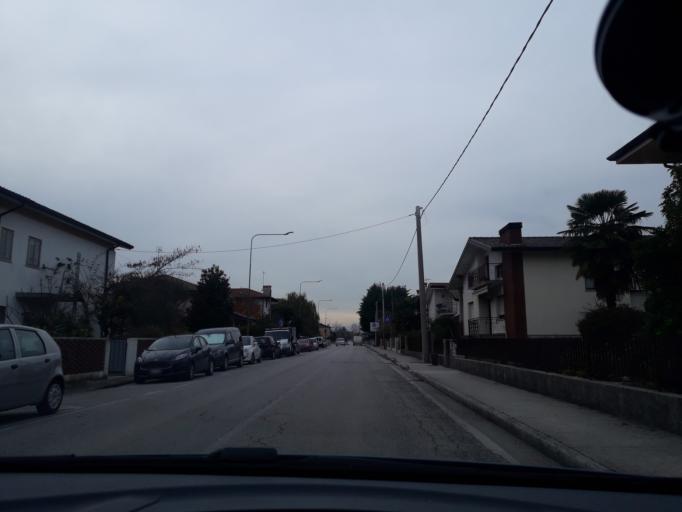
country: IT
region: Friuli Venezia Giulia
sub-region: Provincia di Udine
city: Colugna
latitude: 46.0885
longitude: 13.2033
